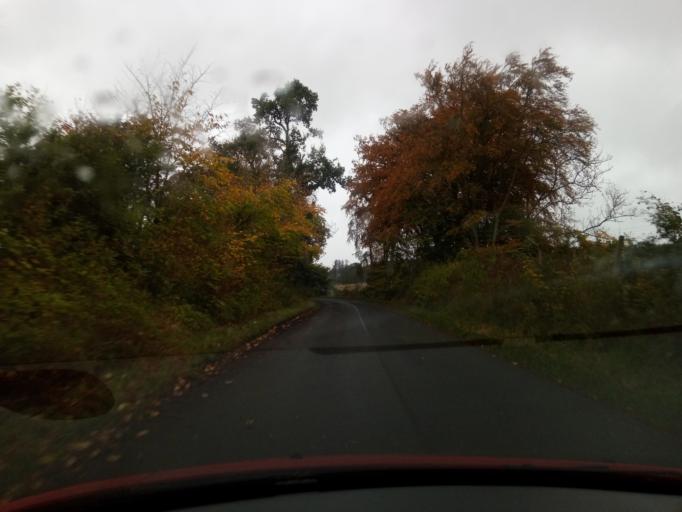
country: GB
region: Scotland
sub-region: The Scottish Borders
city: Selkirk
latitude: 55.5126
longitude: -2.7834
